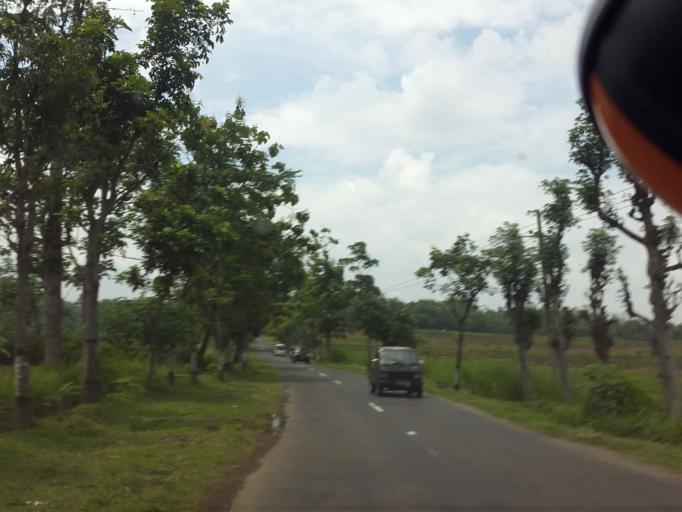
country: ID
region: East Java
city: Madiun
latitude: -7.7080
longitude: 111.3510
